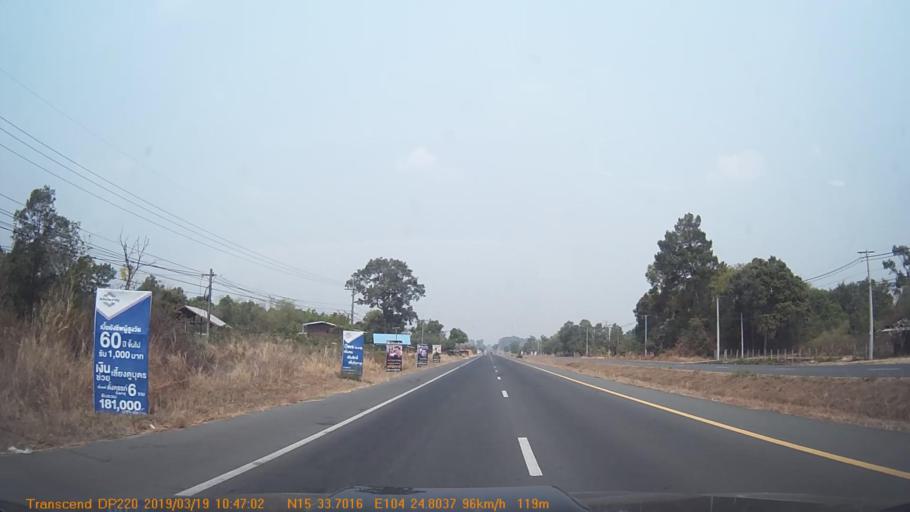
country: TH
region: Yasothon
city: Kham Khuean Kaeo
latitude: 15.5620
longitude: 104.4131
